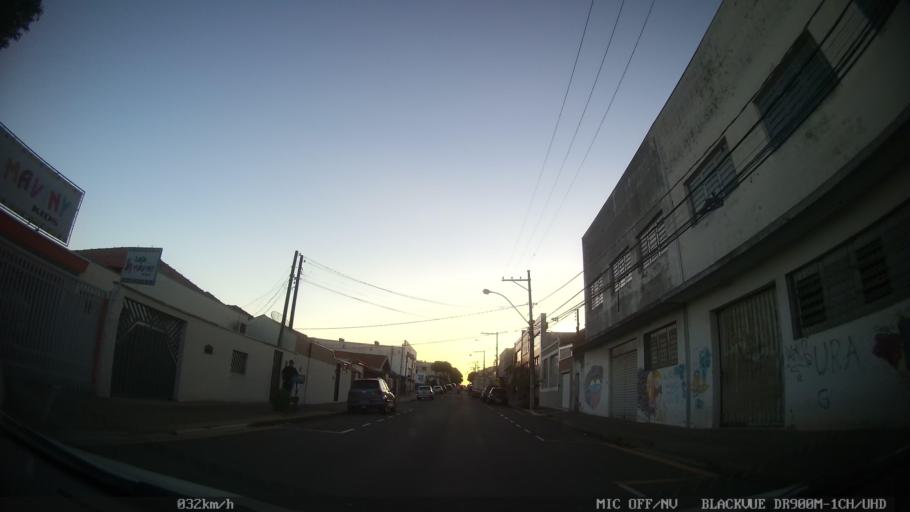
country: BR
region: Sao Paulo
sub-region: Santa Barbara D'Oeste
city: Santa Barbara d'Oeste
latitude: -22.7551
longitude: -47.4218
